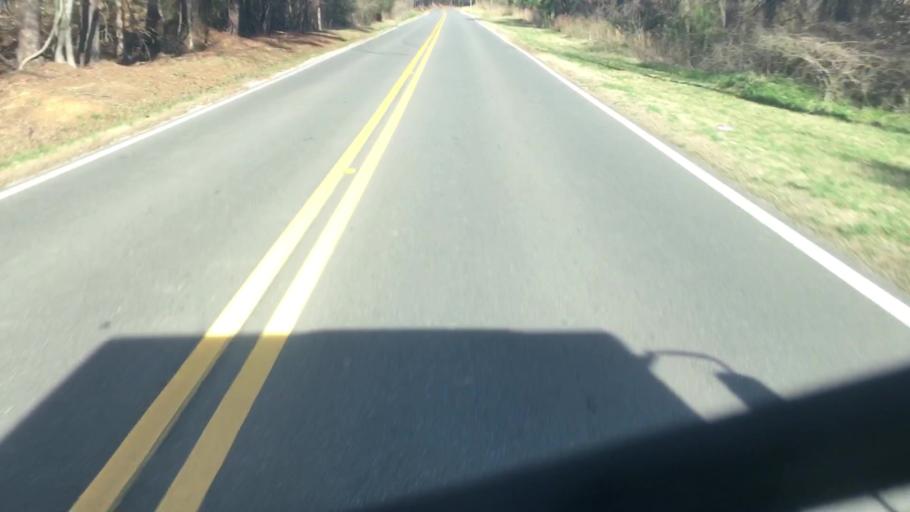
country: US
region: Alabama
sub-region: Jefferson County
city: Cahaba Heights
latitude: 33.4552
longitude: -86.7015
